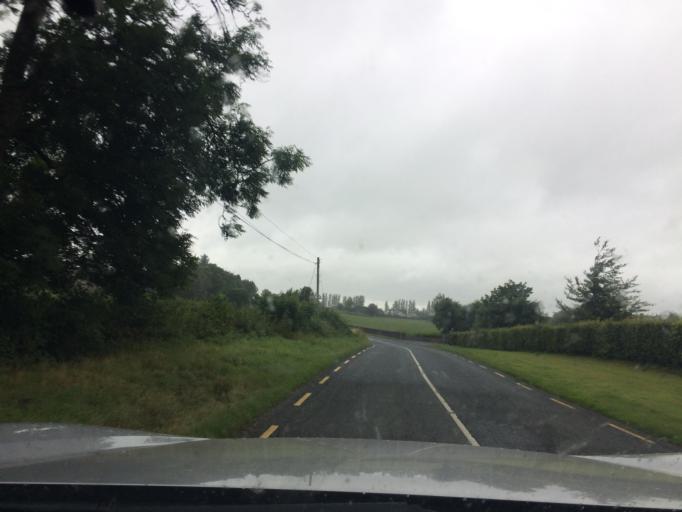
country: IE
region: Munster
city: Cashel
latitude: 52.5331
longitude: -7.8903
